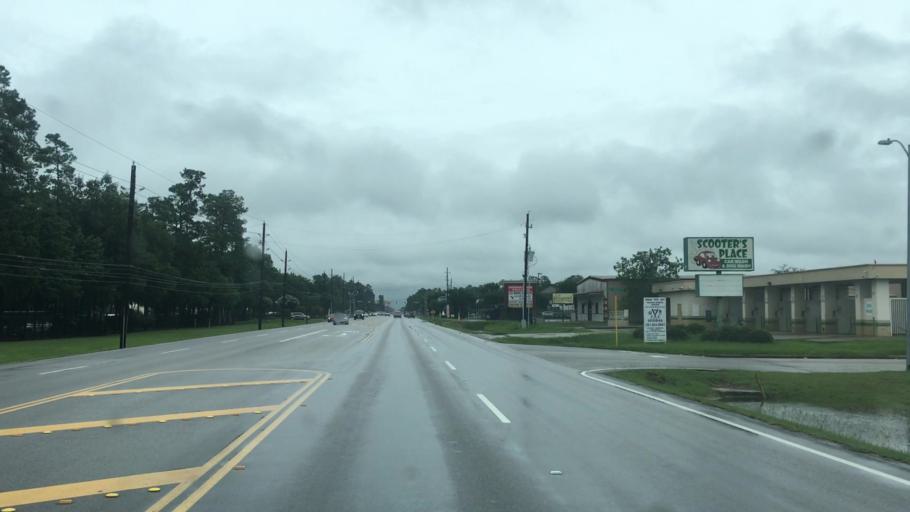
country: US
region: Texas
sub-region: Harris County
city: Atascocita
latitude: 29.9872
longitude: -95.1961
